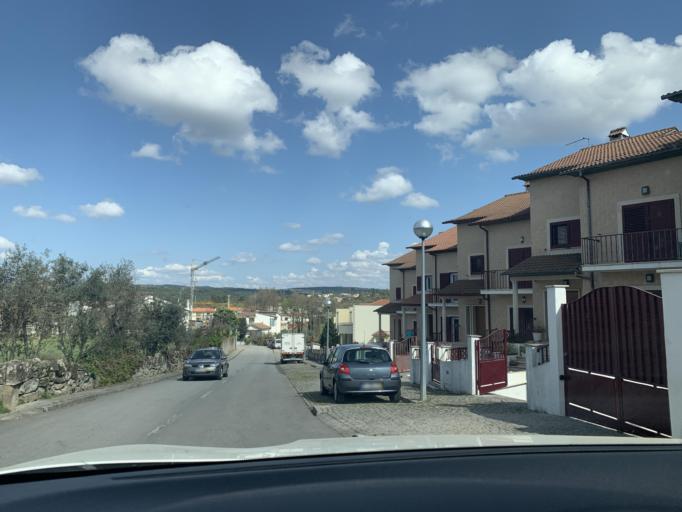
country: PT
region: Viseu
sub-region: Viseu
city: Rio de Loba
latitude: 40.6734
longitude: -7.8814
